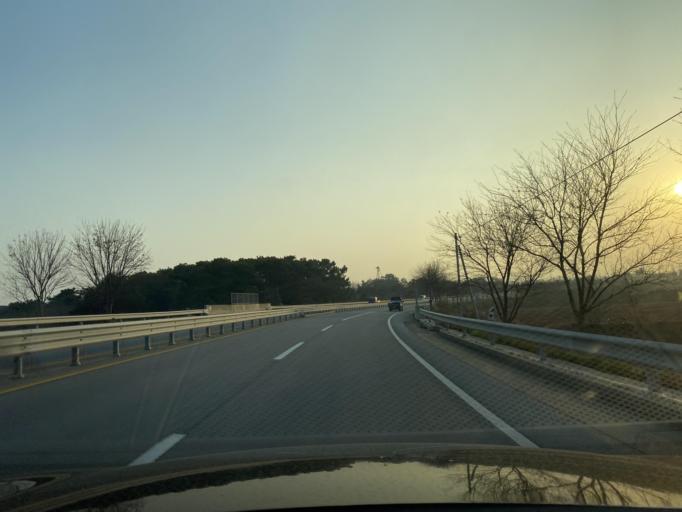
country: KR
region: Chungcheongnam-do
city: Yesan
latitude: 36.6922
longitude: 126.7941
